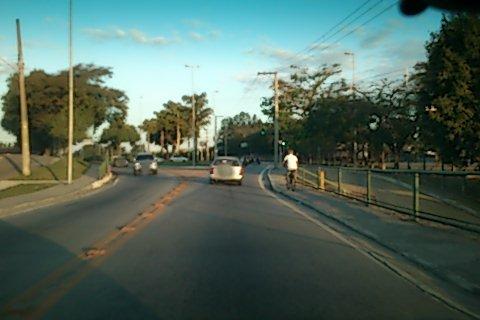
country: BR
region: Sao Paulo
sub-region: Sao Jose Dos Campos
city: Sao Jose dos Campos
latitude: -23.1633
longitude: -45.9022
